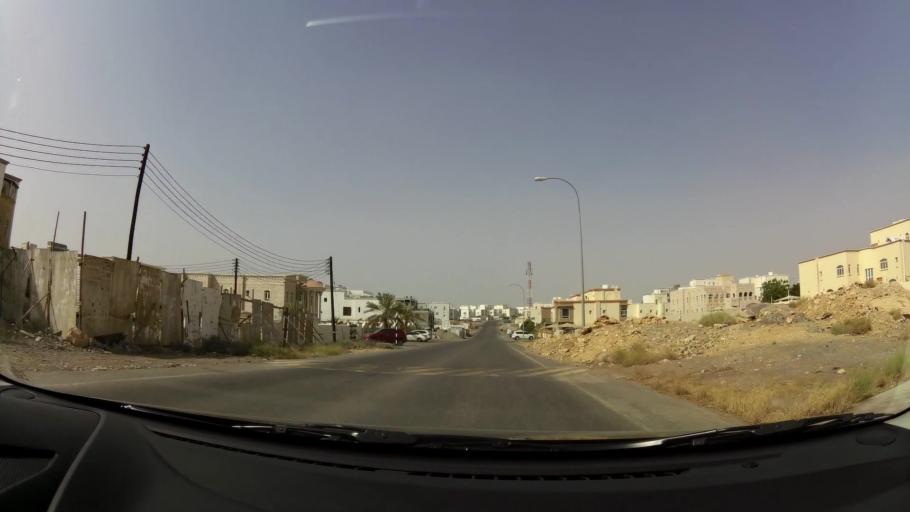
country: OM
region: Muhafazat Masqat
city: Bawshar
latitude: 23.5521
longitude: 58.3494
